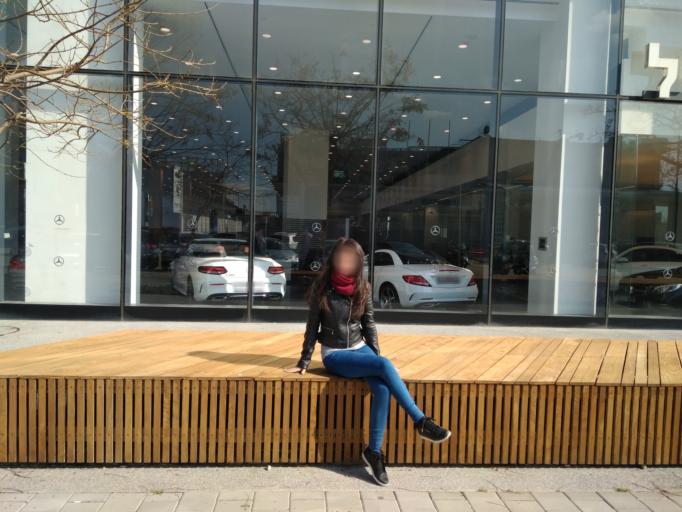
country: IL
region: Tel Aviv
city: Herzliya Pituah
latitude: 32.1592
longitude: 34.8058
